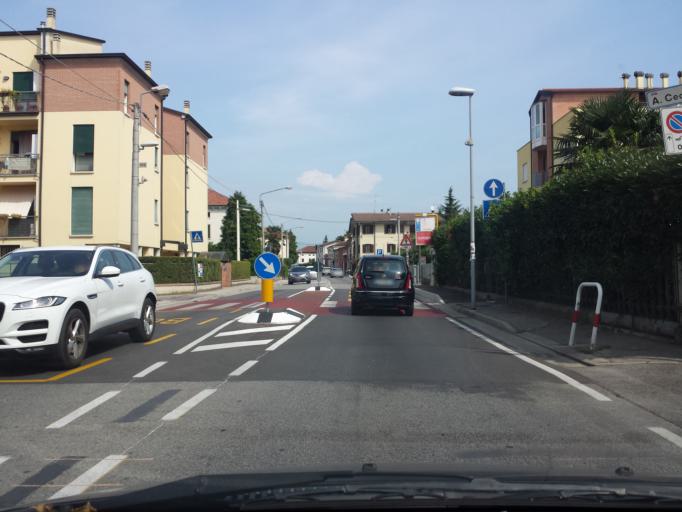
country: IT
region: Veneto
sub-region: Provincia di Vicenza
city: Monticello Conte Otto
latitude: 45.5888
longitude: 11.5570
